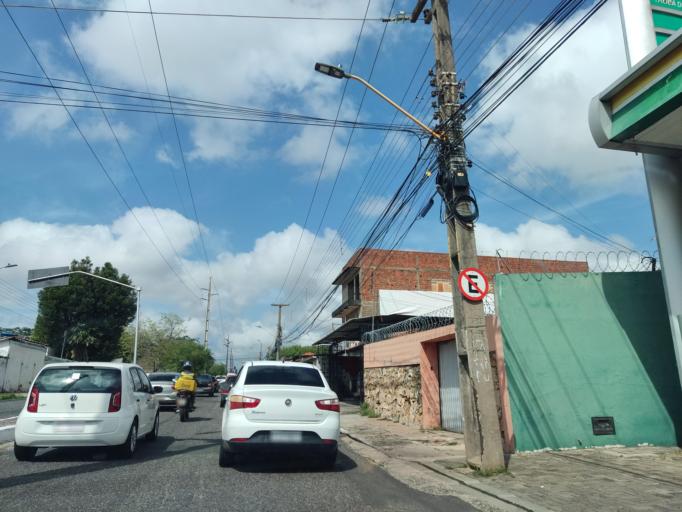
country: BR
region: Piaui
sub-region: Teresina
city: Teresina
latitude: -5.0737
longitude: -42.8108
